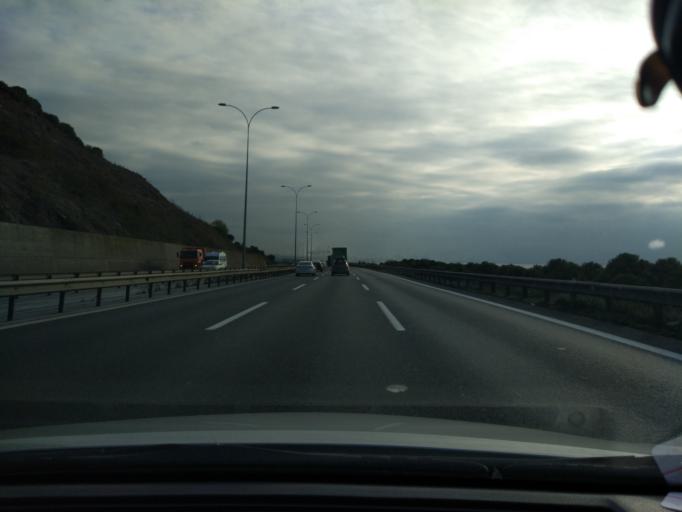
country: TR
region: Kocaeli
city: Hereke
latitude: 40.7794
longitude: 29.6727
